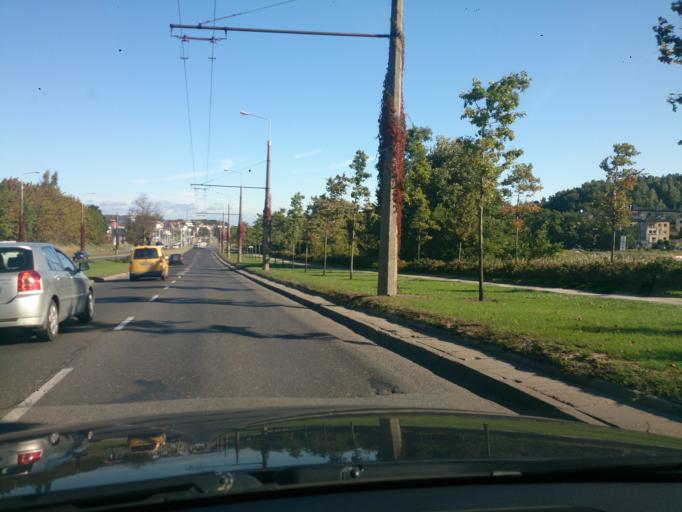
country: PL
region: Pomeranian Voivodeship
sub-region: Gdynia
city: Wielki Kack
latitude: 54.4698
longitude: 18.5112
